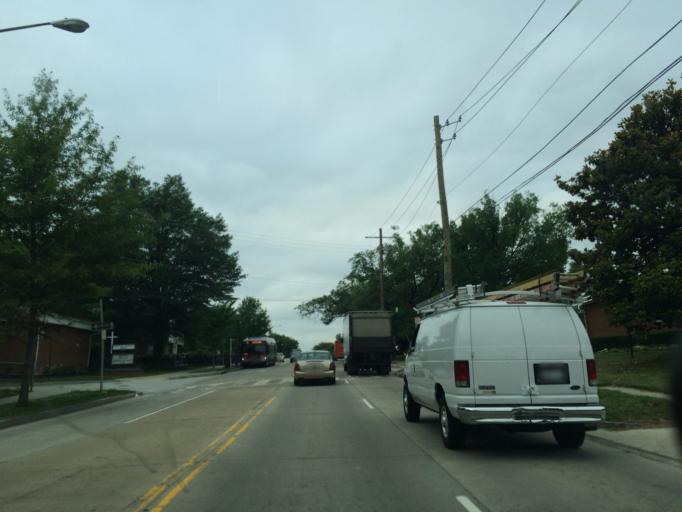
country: US
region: Maryland
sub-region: Prince George's County
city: Chillum
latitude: 38.9624
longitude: -77.0050
